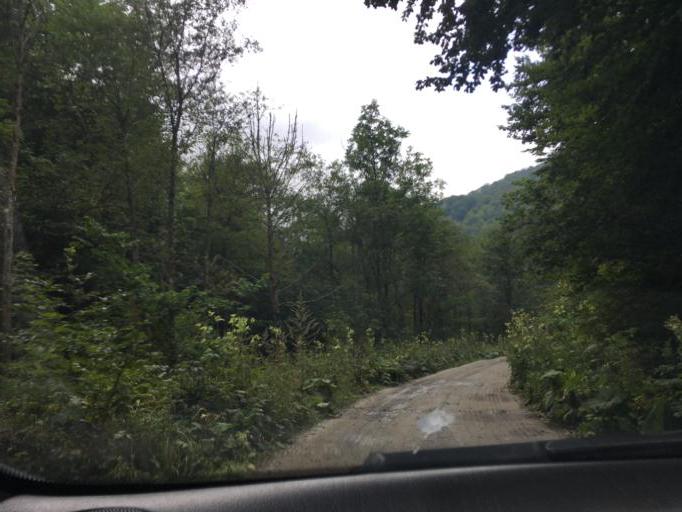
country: PL
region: Subcarpathian Voivodeship
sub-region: Powiat bieszczadzki
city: Lutowiska
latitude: 49.1849
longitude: 22.6181
